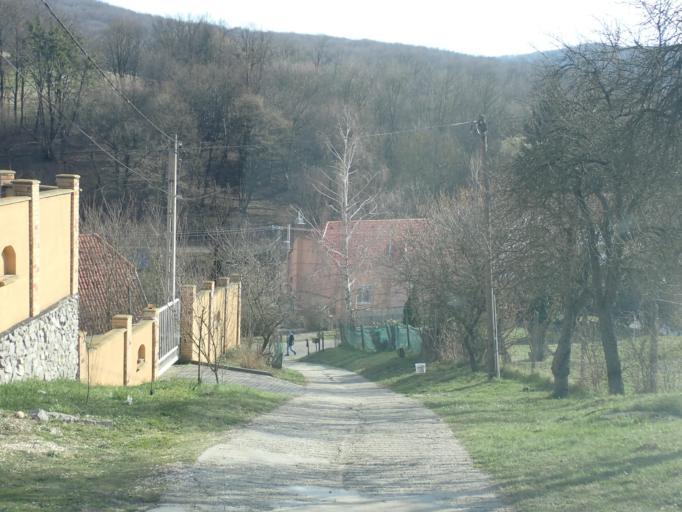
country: HU
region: Baranya
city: Komlo
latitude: 46.1623
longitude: 18.2486
